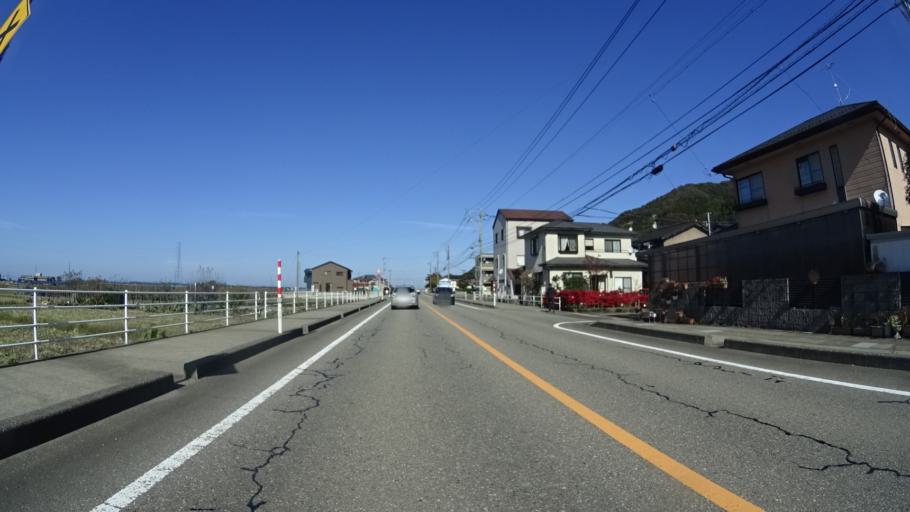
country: JP
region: Ishikawa
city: Tsurugi-asahimachi
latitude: 36.4587
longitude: 136.6220
